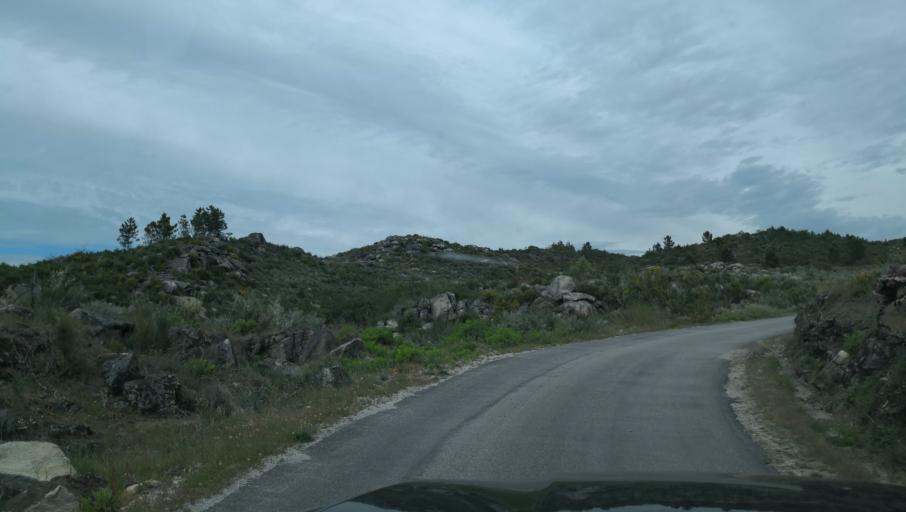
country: PT
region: Vila Real
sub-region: Vila Real
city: Vila Real
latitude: 41.3656
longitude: -7.6991
